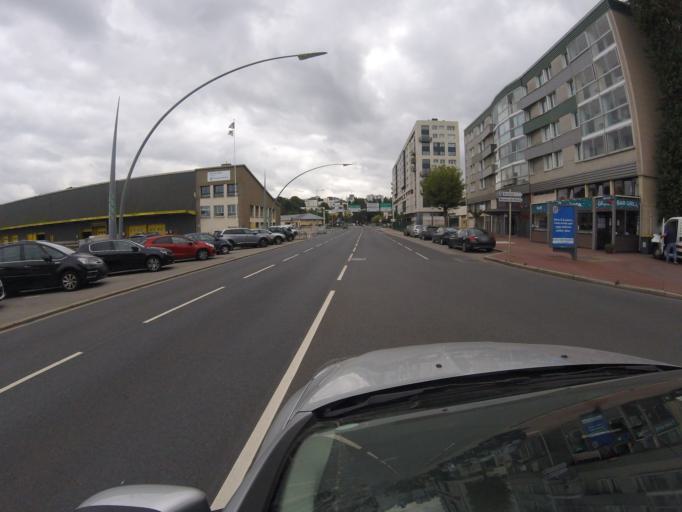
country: FR
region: Lower Normandy
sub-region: Departement de la Manche
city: Cherbourg-Octeville
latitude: 49.6353
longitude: -1.6221
